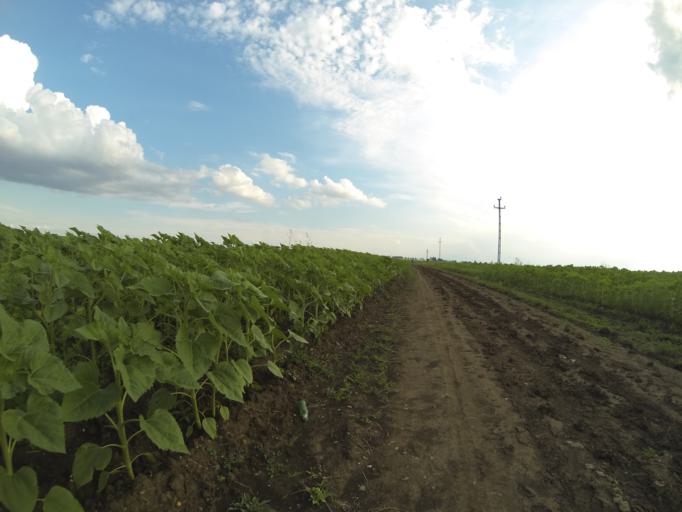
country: RO
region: Dolj
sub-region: Comuna Caloparu
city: Salcuta
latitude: 44.1511
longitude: 23.7034
